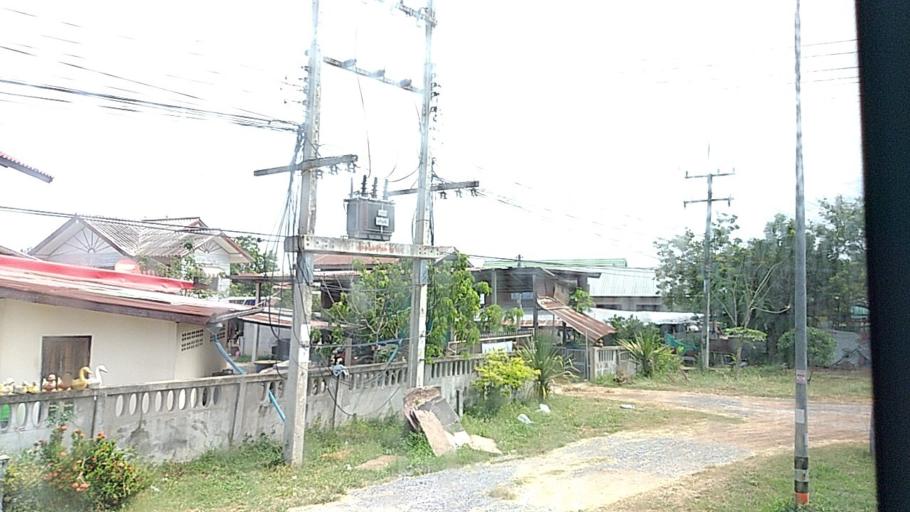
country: TH
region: Maha Sarakham
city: Chiang Yuen
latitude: 16.3665
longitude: 103.1060
